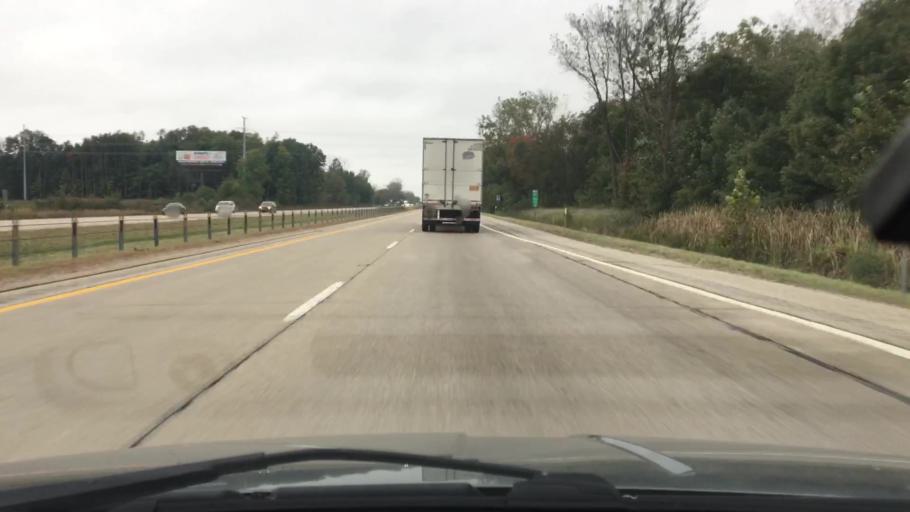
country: US
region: Michigan
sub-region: Van Buren County
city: Hartford
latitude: 42.1919
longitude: -86.1731
